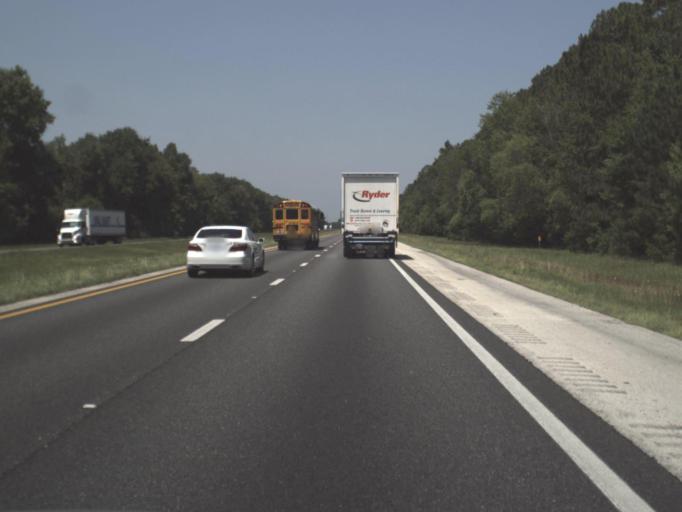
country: US
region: Florida
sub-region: Duval County
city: Baldwin
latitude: 30.3035
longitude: -81.9090
